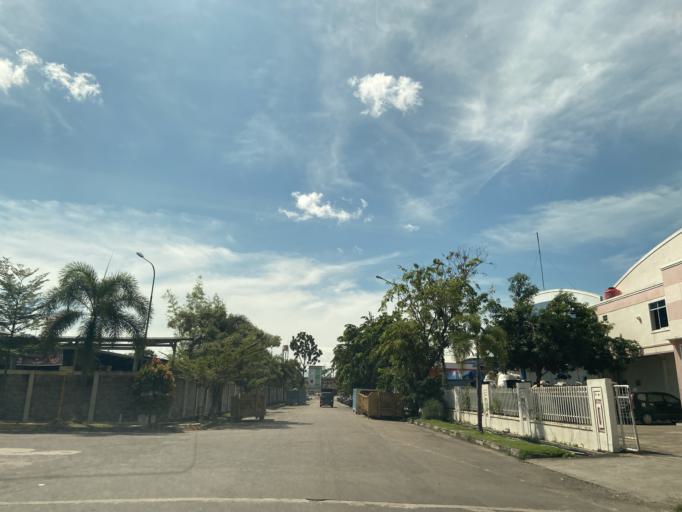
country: SG
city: Singapore
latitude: 1.1100
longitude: 104.0684
